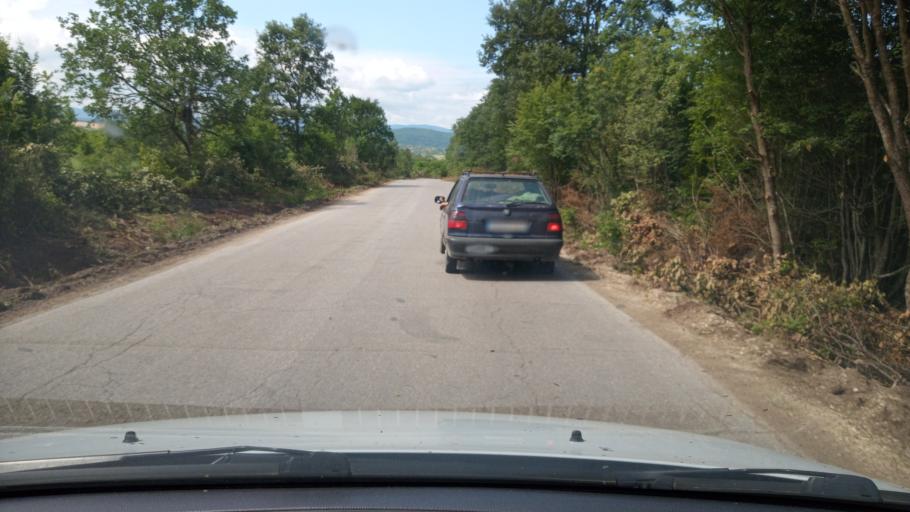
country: BG
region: Lovech
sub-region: Obshtina Lukovit
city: Lukovit
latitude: 43.1914
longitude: 24.0961
